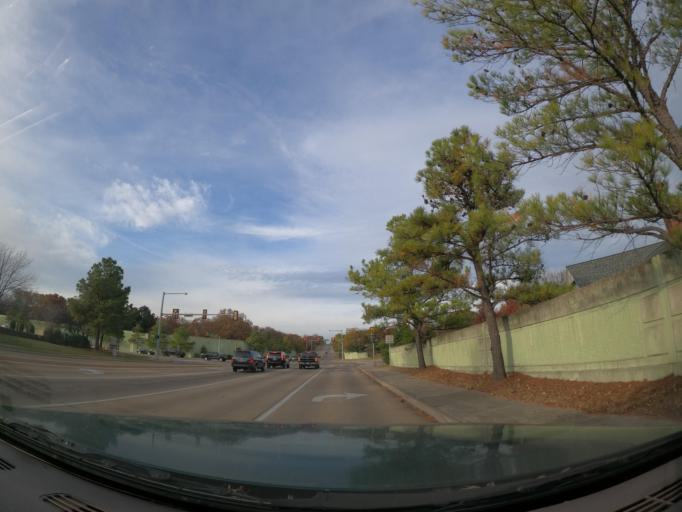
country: US
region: Oklahoma
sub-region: Tulsa County
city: Jenks
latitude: 36.0603
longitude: -95.9398
